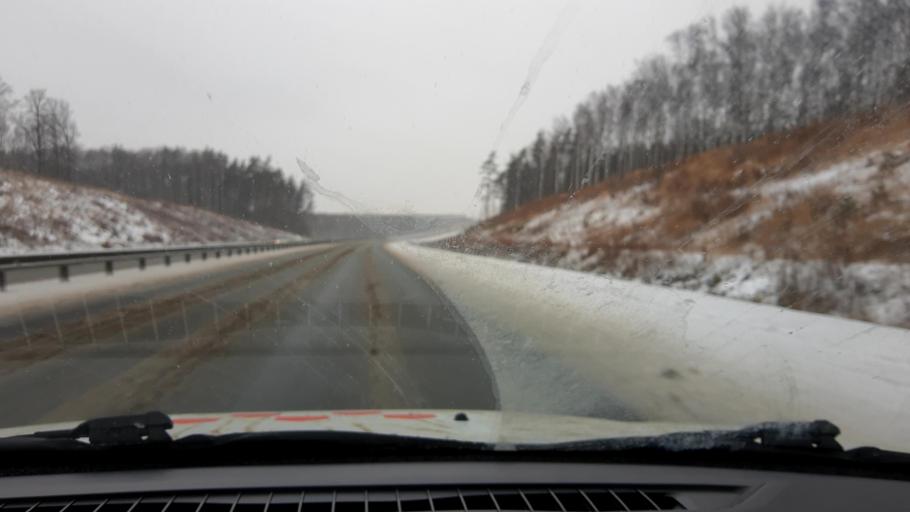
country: RU
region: Nizjnij Novgorod
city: Afonino
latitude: 56.1011
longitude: 44.0295
